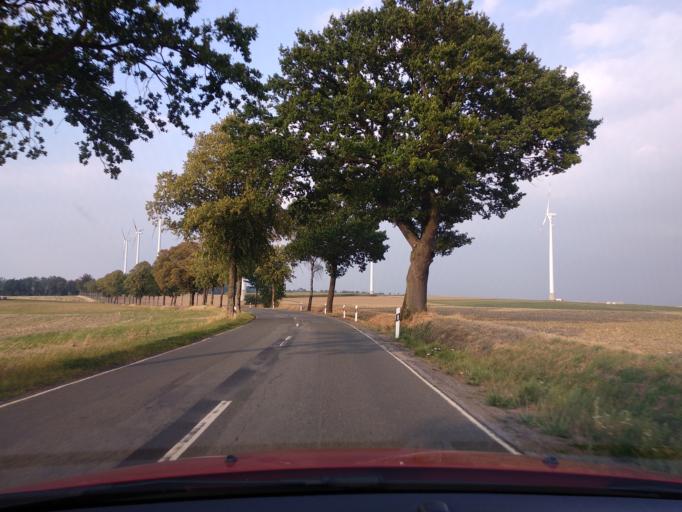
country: DE
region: North Rhine-Westphalia
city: Borgentreich
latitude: 51.5918
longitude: 9.3229
